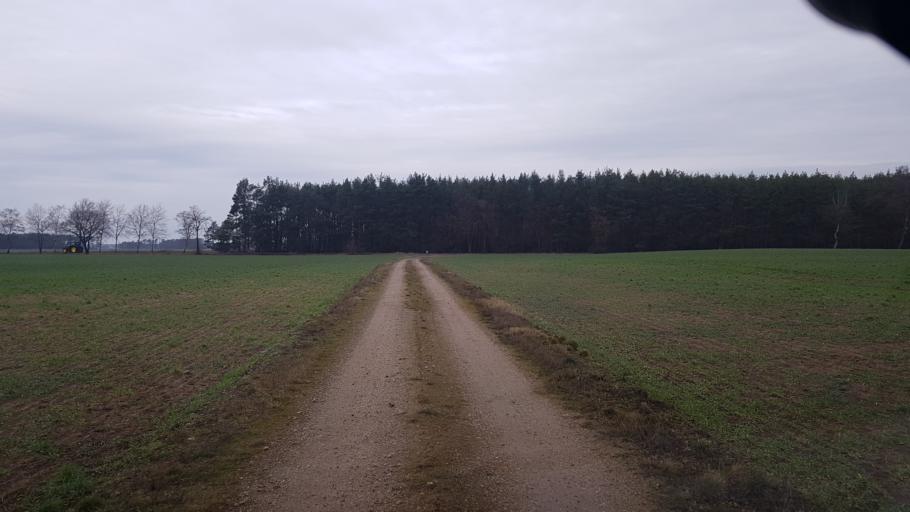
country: DE
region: Brandenburg
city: Bad Liebenwerda
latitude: 51.5365
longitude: 13.3332
